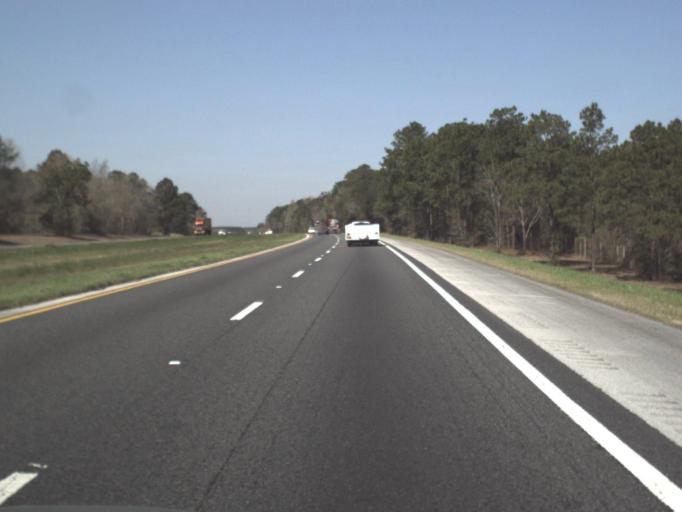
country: US
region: Florida
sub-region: Jackson County
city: Sneads
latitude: 30.6791
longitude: -85.0848
